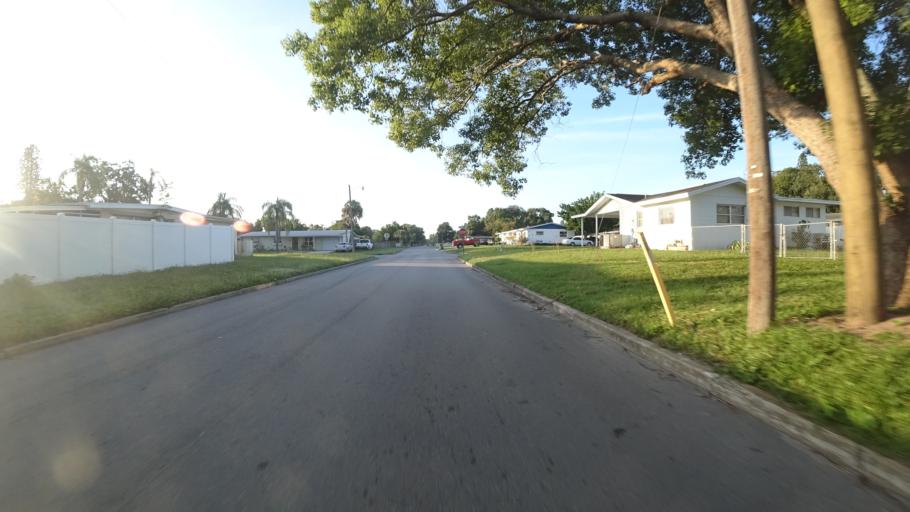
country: US
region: Florida
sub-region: Manatee County
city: South Bradenton
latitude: 27.4781
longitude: -82.5836
